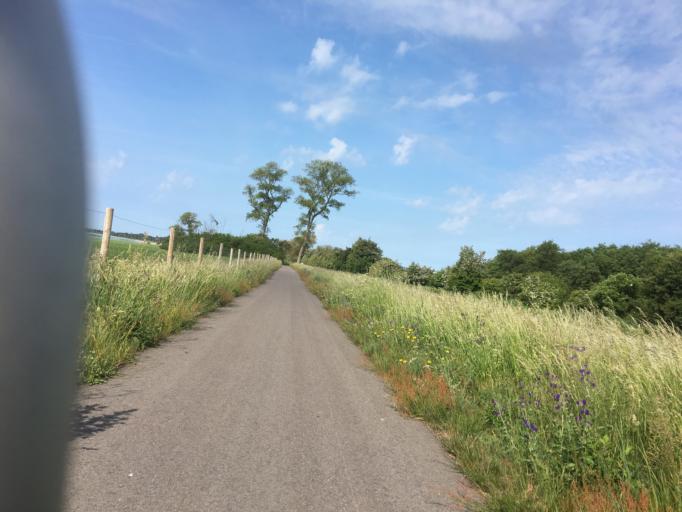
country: SE
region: Skane
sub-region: Skurups Kommun
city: Skivarp
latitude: 55.3871
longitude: 13.5218
